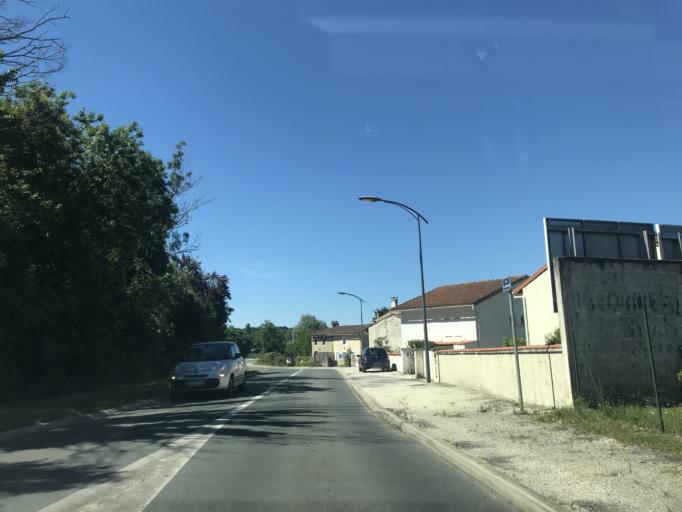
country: FR
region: Poitou-Charentes
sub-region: Departement de la Charente-Maritime
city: Gemozac
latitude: 45.5662
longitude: -0.7194
